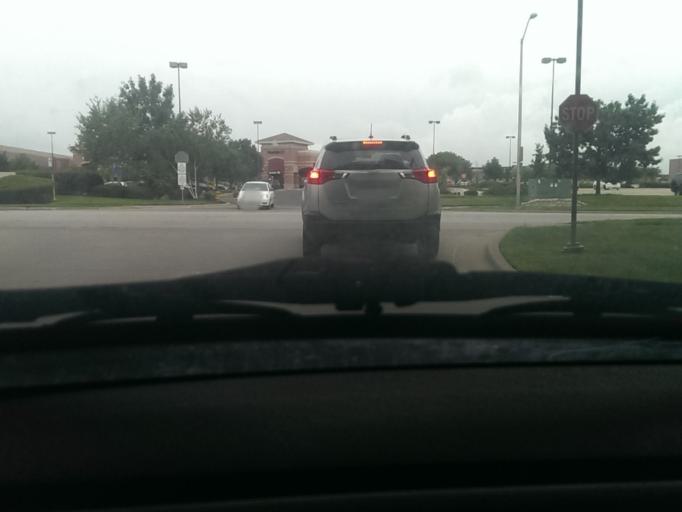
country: US
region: Kansas
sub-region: Johnson County
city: Leawood
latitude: 38.9169
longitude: -94.6462
